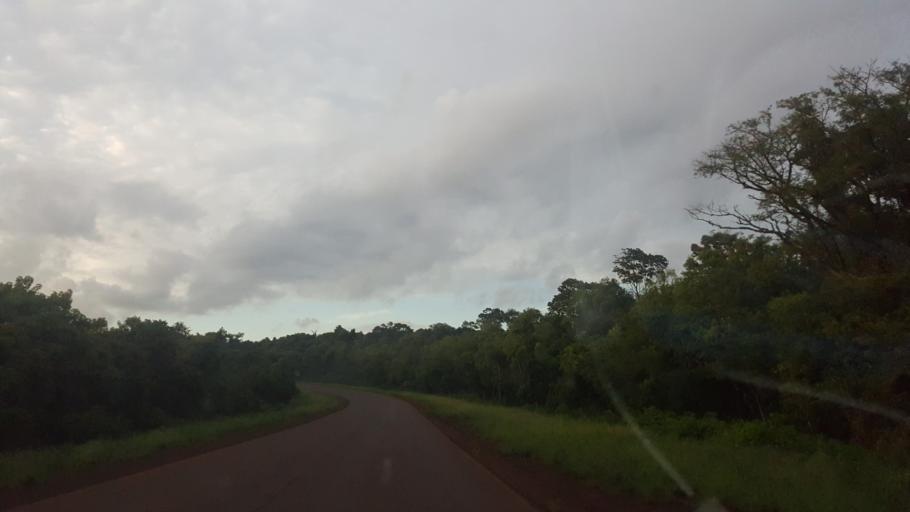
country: AR
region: Misiones
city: Dos de Mayo
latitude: -26.9330
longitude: -54.7193
